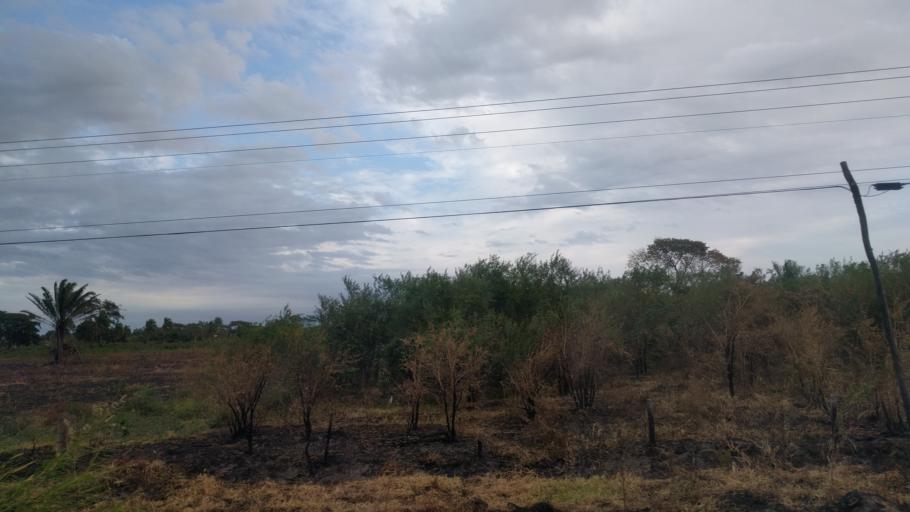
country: BO
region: Santa Cruz
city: Montero
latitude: -17.3949
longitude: -63.2137
